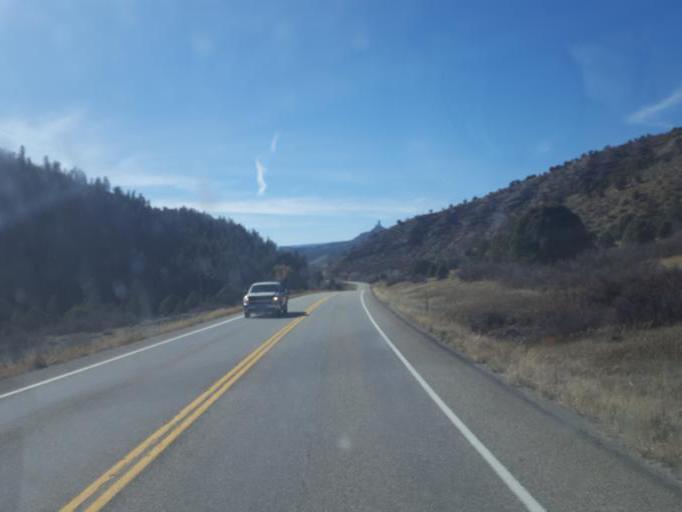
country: US
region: Colorado
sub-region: Archuleta County
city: Pagosa Springs
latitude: 37.2120
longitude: -107.2330
